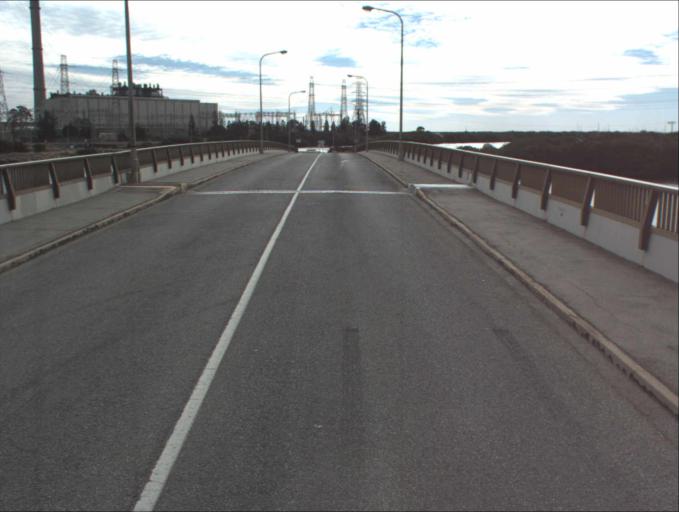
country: AU
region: South Australia
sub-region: Port Adelaide Enfield
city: Birkenhead
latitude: -34.8119
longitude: 138.5253
